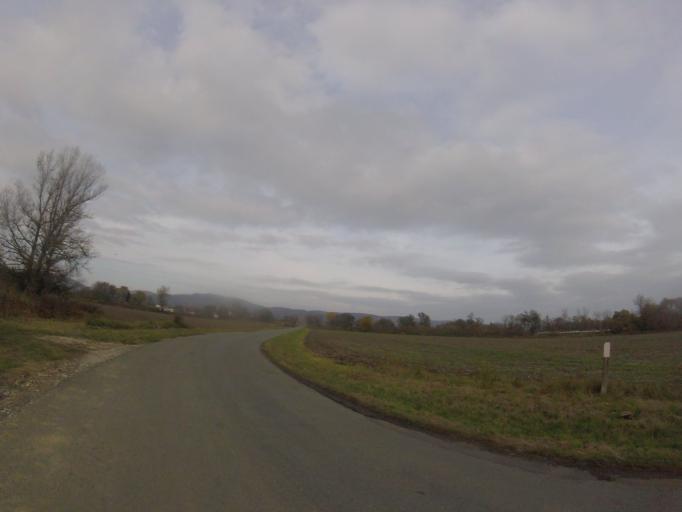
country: HU
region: Borsod-Abauj-Zemplen
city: Putnok
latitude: 48.2809
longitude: 20.4385
